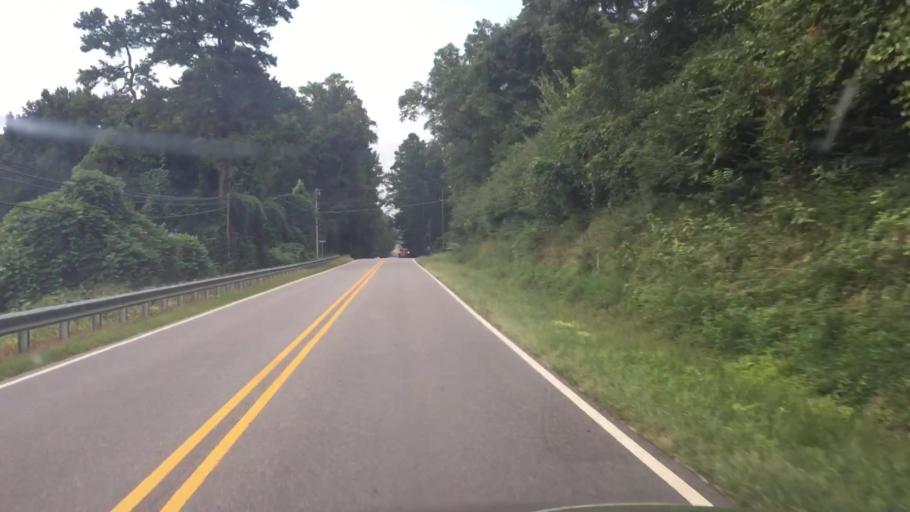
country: US
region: North Carolina
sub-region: Iredell County
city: Mooresville
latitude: 35.5933
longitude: -80.7990
